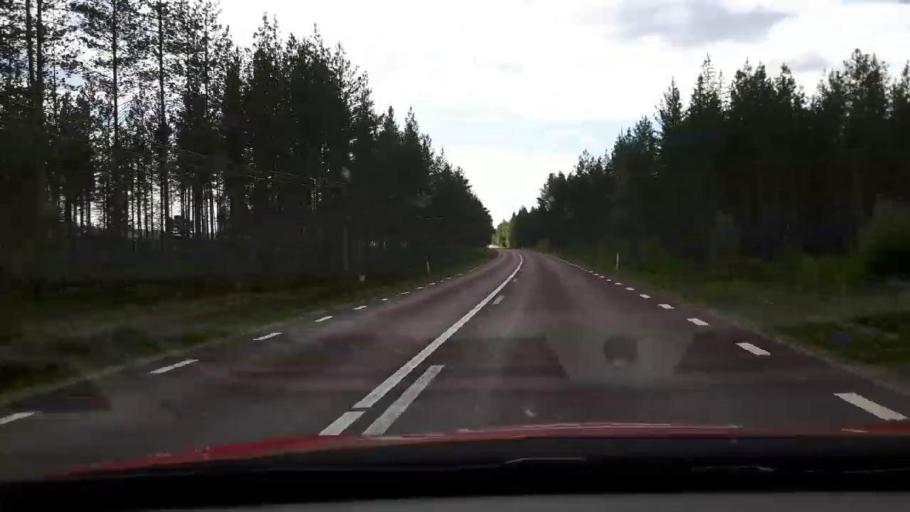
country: SE
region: Jaemtland
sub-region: Harjedalens Kommun
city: Sveg
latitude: 62.1194
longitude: 14.9700
